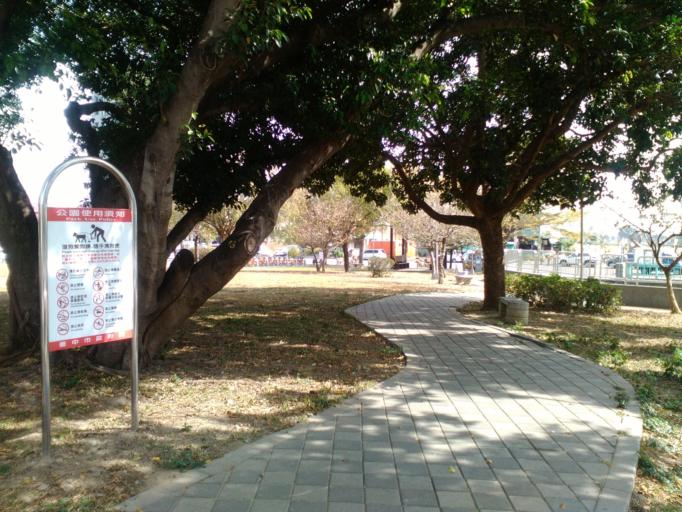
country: TW
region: Taiwan
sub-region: Taichung City
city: Taichung
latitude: 24.1154
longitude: 120.6709
